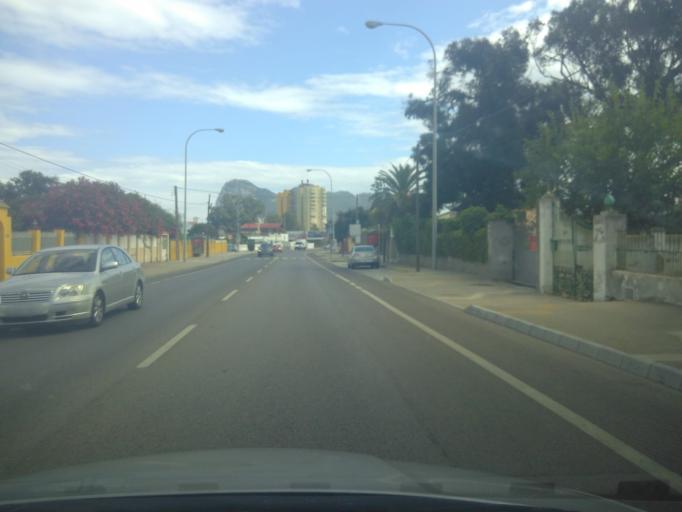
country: ES
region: Andalusia
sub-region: Provincia de Cadiz
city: La Linea de la Concepcion
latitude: 36.1727
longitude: -5.3723
